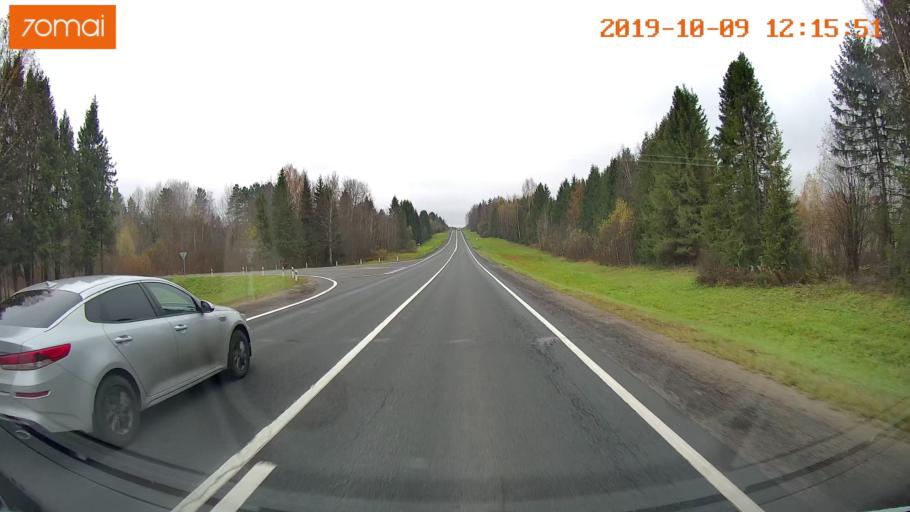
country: RU
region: Jaroslavl
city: Prechistoye
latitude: 58.4773
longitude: 40.3223
